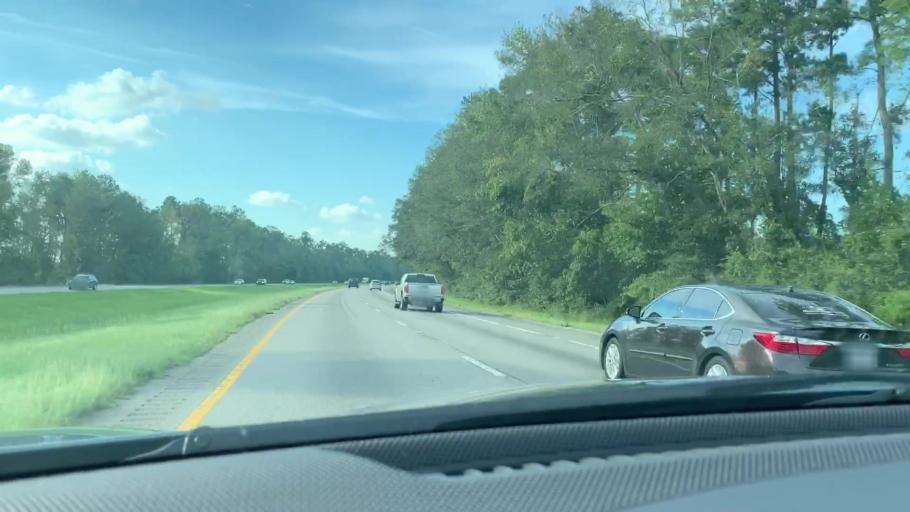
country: US
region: South Carolina
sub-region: Orangeburg County
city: Brookdale
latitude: 33.4736
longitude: -80.7503
